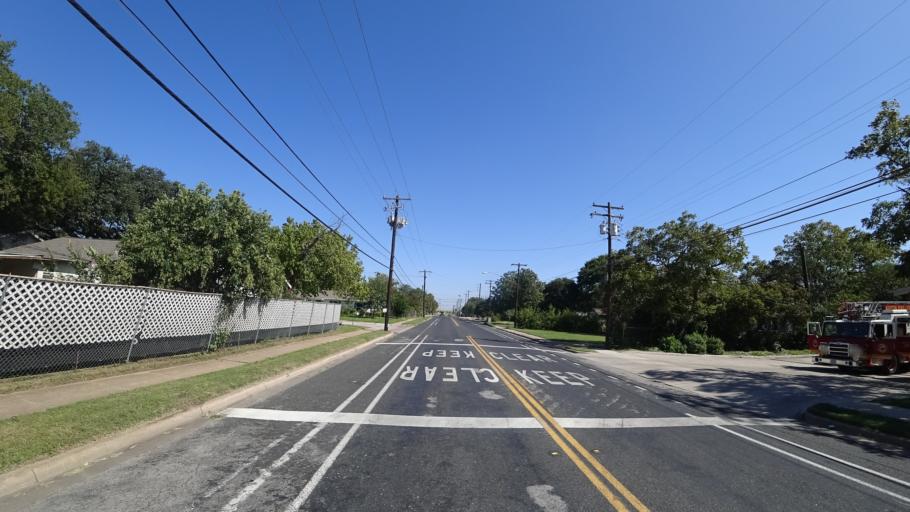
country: US
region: Texas
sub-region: Travis County
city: Austin
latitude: 30.3174
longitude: -97.6905
